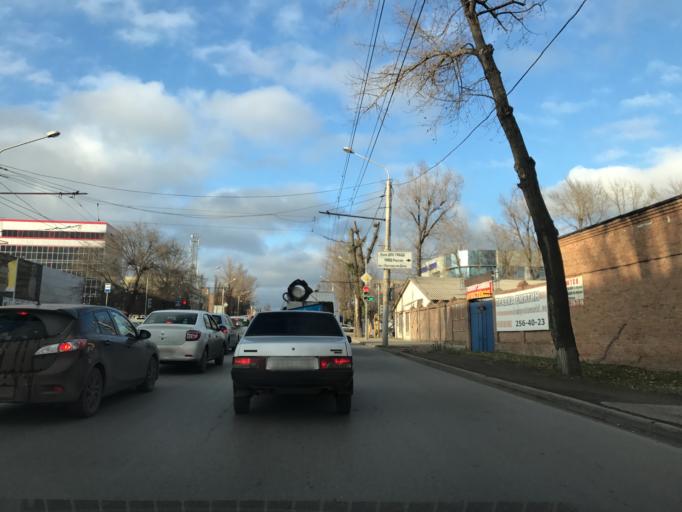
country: RU
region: Rostov
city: Severnyy
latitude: 47.2763
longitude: 39.6863
